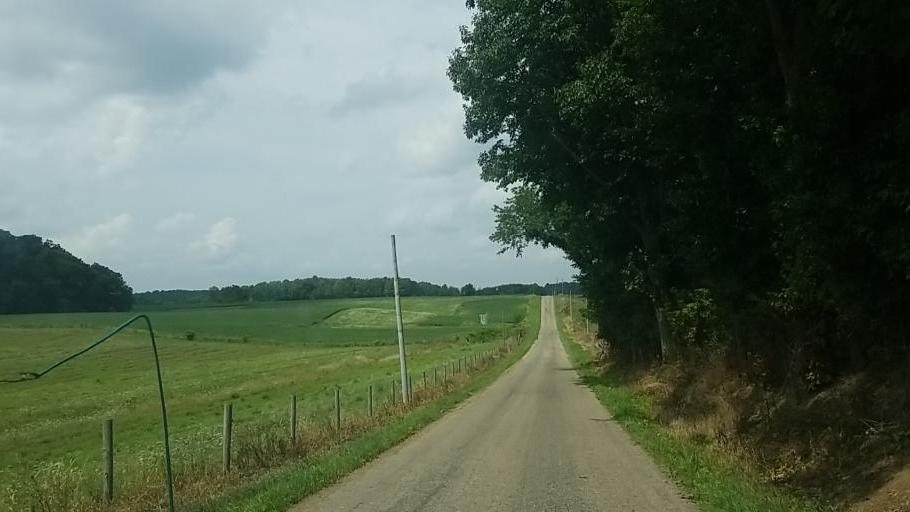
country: US
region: Ohio
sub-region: Knox County
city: Gambier
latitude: 40.2626
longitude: -82.3029
